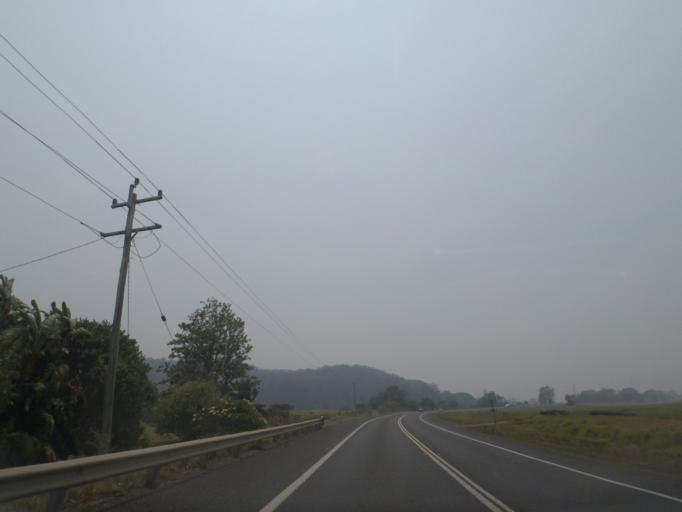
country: AU
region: New South Wales
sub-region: Clarence Valley
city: Maclean
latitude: -29.5422
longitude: 153.1574
